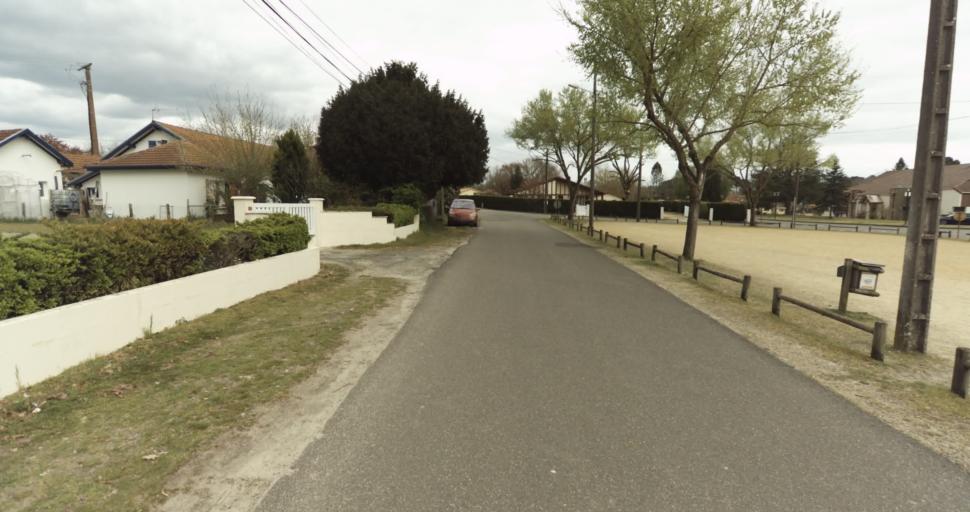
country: FR
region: Aquitaine
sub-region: Departement des Landes
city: Roquefort
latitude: 44.0336
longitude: -0.3162
